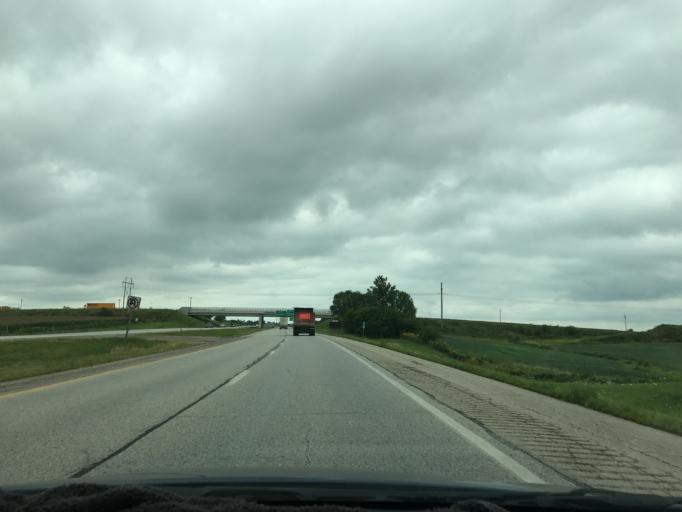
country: US
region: Iowa
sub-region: Scott County
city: Bettendorf
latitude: 41.5872
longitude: -90.5222
